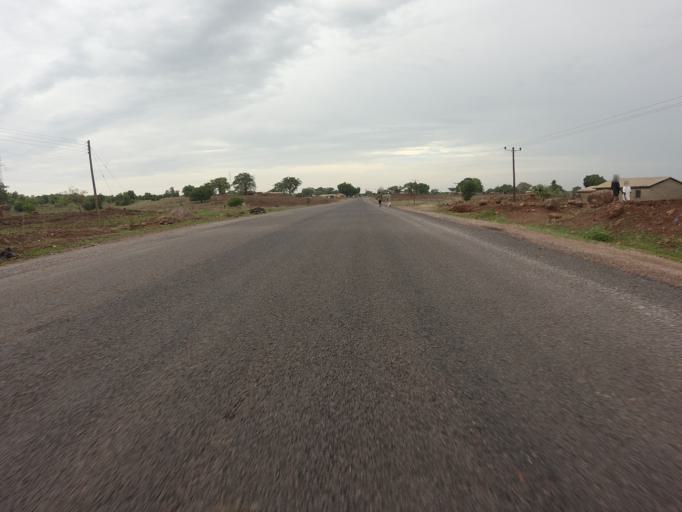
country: GH
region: Upper East
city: Bolgatanga
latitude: 10.8495
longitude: -0.6787
